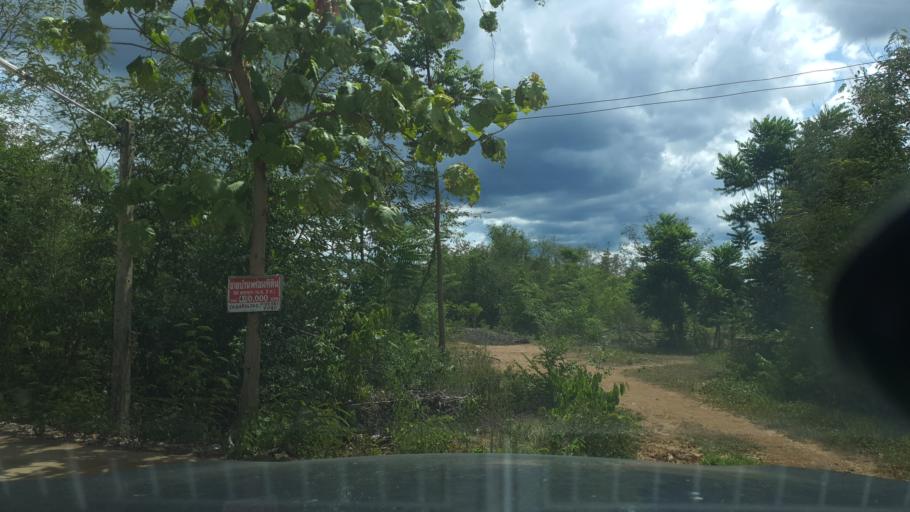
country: TH
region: Sukhothai
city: Thung Saliam
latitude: 17.3293
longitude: 99.5456
